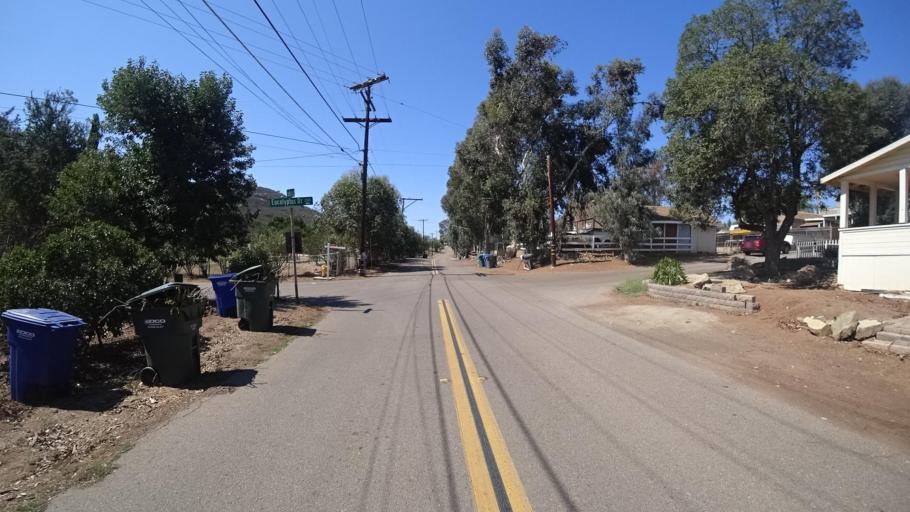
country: US
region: California
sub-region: San Diego County
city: Crest
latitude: 32.8006
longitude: -116.8652
